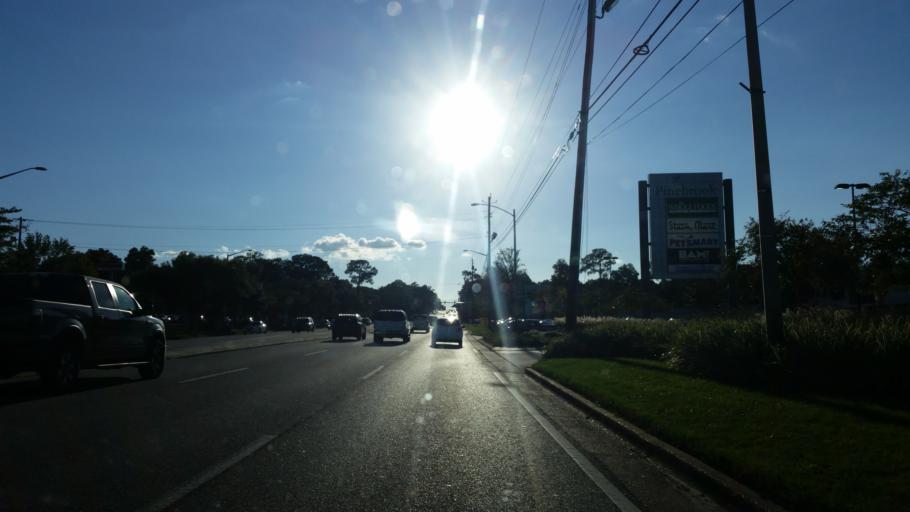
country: US
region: Alabama
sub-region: Mobile County
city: Tillmans Corner
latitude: 30.6762
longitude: -88.1495
